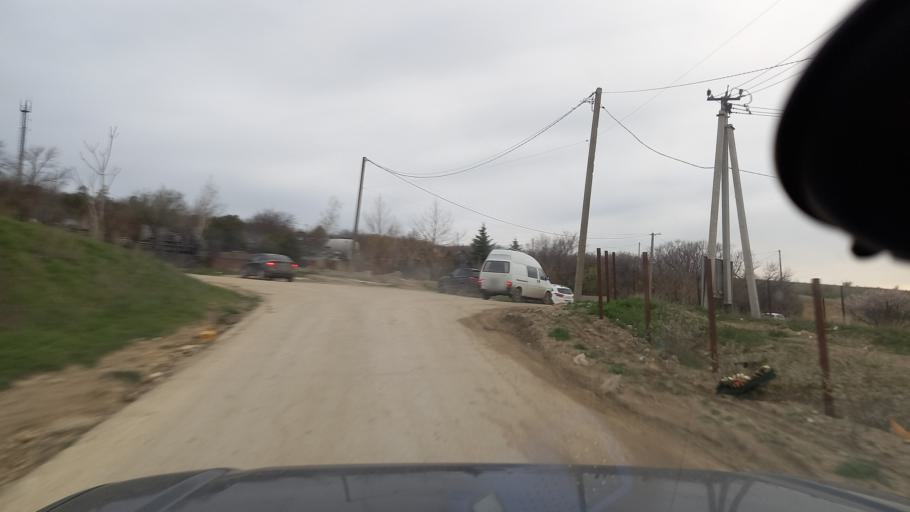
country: RU
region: Krasnodarskiy
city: Anapa
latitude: 44.8497
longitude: 37.3458
